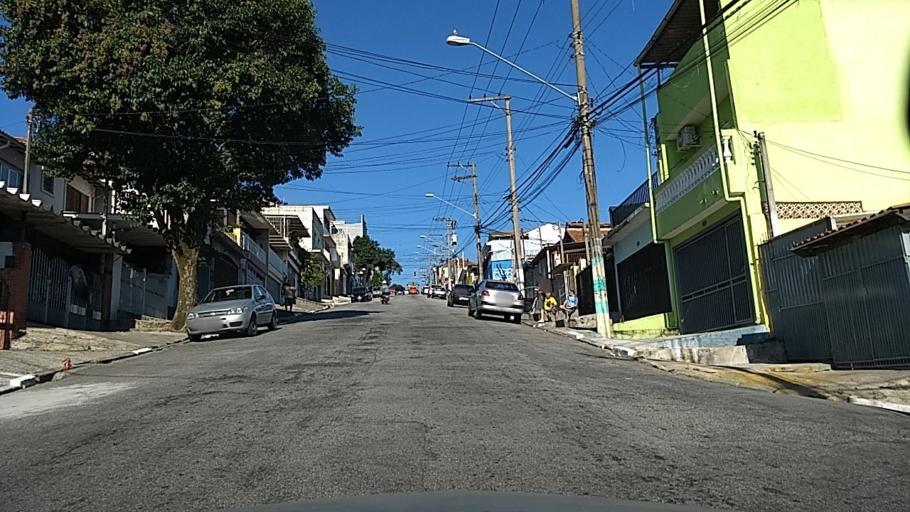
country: BR
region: Sao Paulo
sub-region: Guarulhos
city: Guarulhos
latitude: -23.4897
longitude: -46.5872
